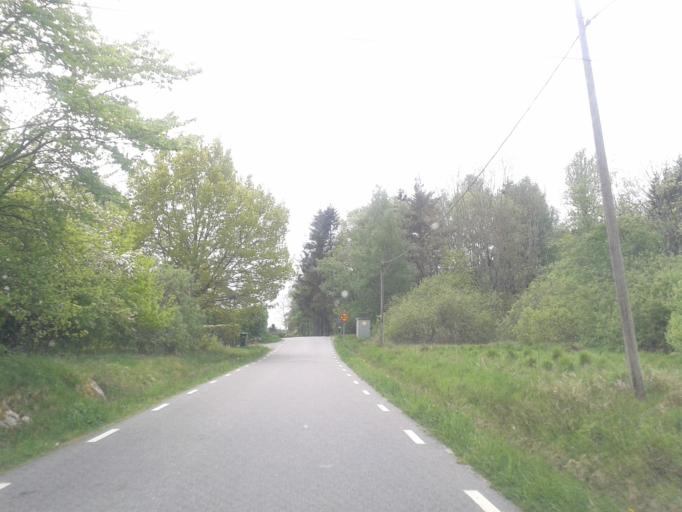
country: SE
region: Vaestra Goetaland
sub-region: Kungalvs Kommun
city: Kungalv
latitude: 57.8568
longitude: 11.9503
